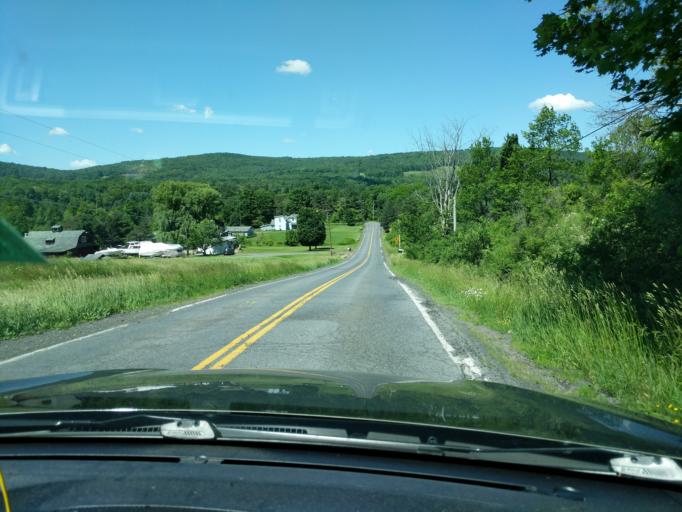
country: US
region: New York
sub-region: Tompkins County
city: East Ithaca
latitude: 42.3716
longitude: -76.3968
